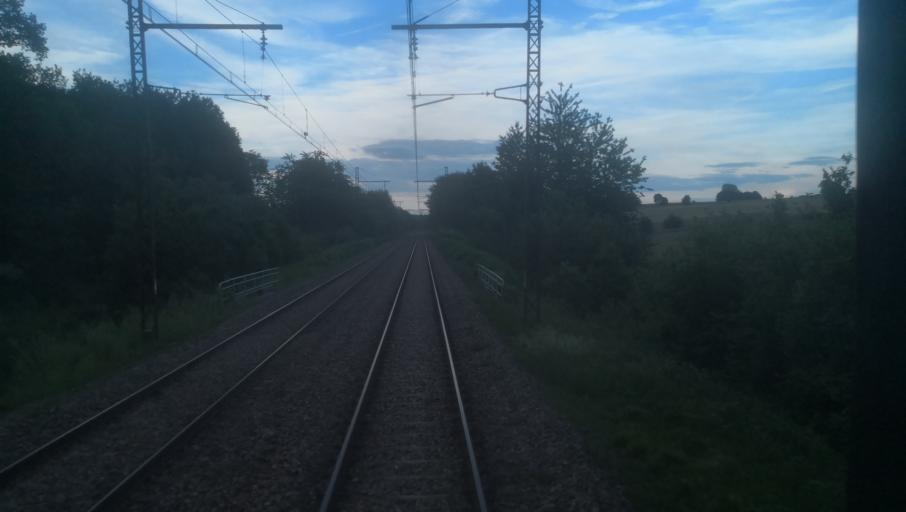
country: FR
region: Limousin
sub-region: Departement de la Creuse
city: Saint-Maurice-la-Souterraine
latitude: 46.1893
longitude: 1.4622
